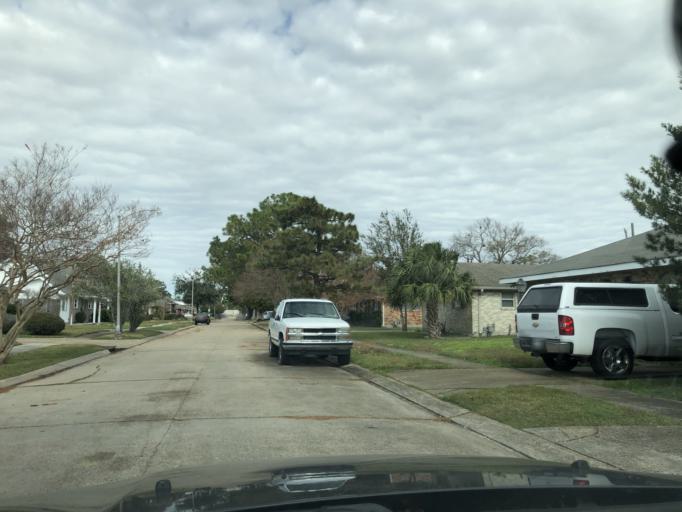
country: US
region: Louisiana
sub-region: Jefferson Parish
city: Metairie Terrace
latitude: 29.9935
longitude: -90.1687
